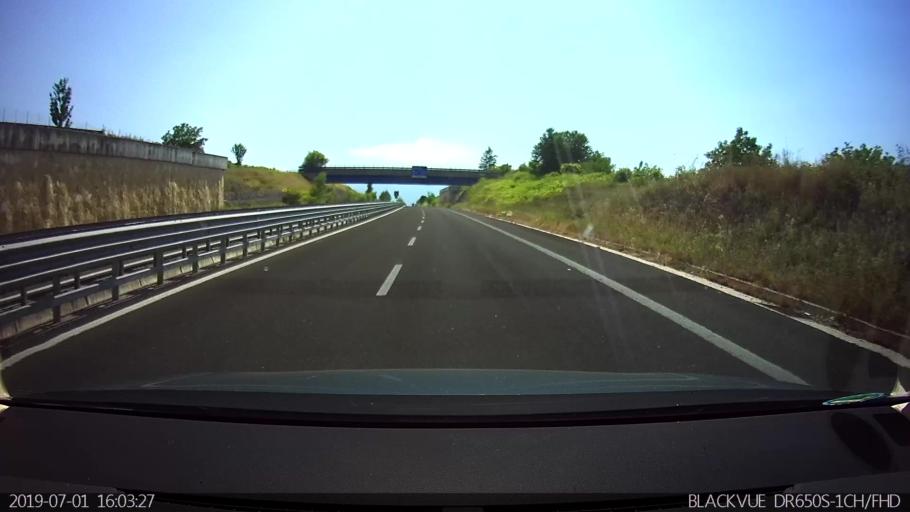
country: IT
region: Latium
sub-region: Provincia di Frosinone
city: Tecchiena
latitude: 41.6732
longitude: 13.3329
